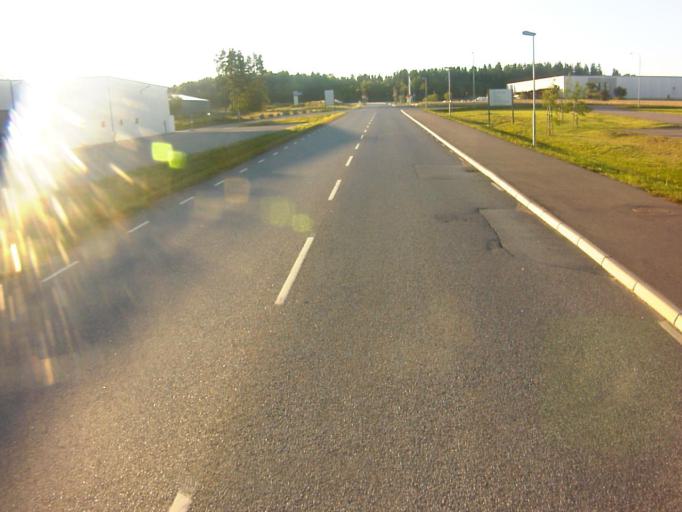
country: SE
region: Soedermanland
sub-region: Eskilstuna Kommun
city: Hallbybrunn
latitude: 59.4016
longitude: 16.4419
